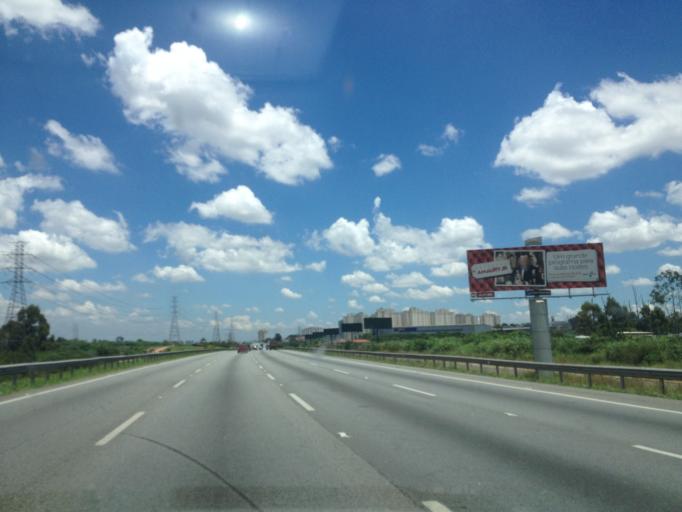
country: BR
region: Sao Paulo
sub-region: Guarulhos
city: Guarulhos
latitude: -23.4882
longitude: -46.5323
